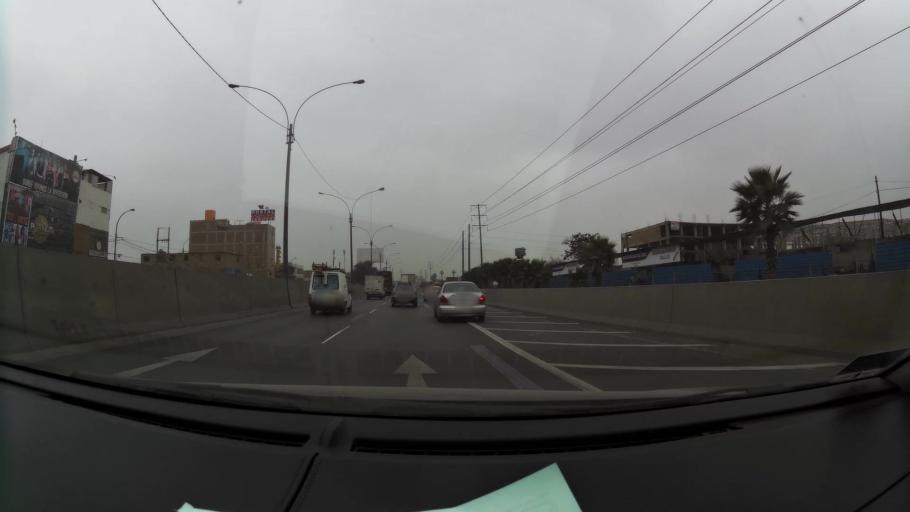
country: PE
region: Lima
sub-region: Lima
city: Carabayllo
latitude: -11.8710
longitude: -77.0702
